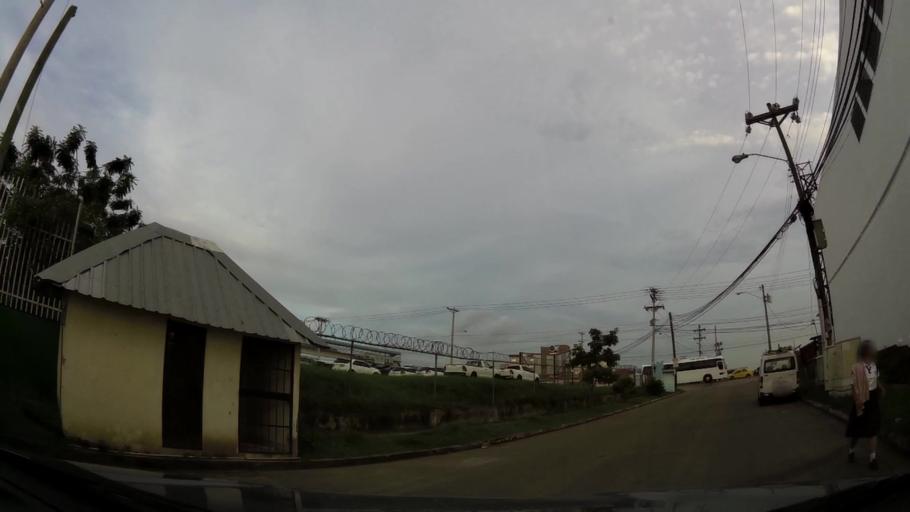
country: PA
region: Panama
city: Tocumen
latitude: 9.0944
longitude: -79.3947
